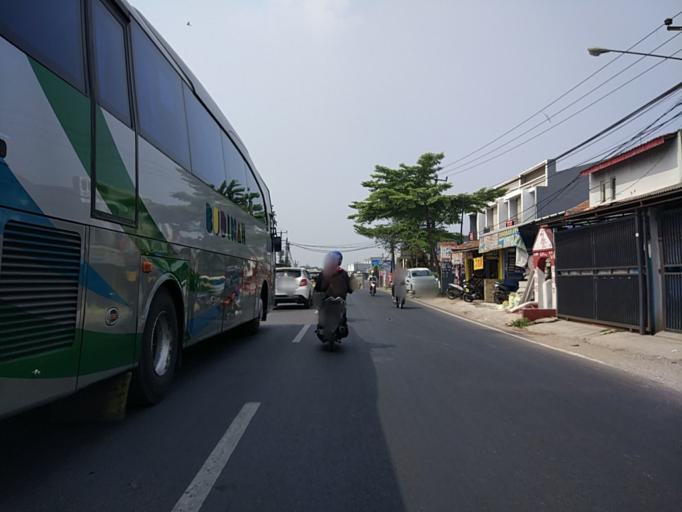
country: ID
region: West Java
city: Padalarang
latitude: -6.8373
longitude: 107.4731
